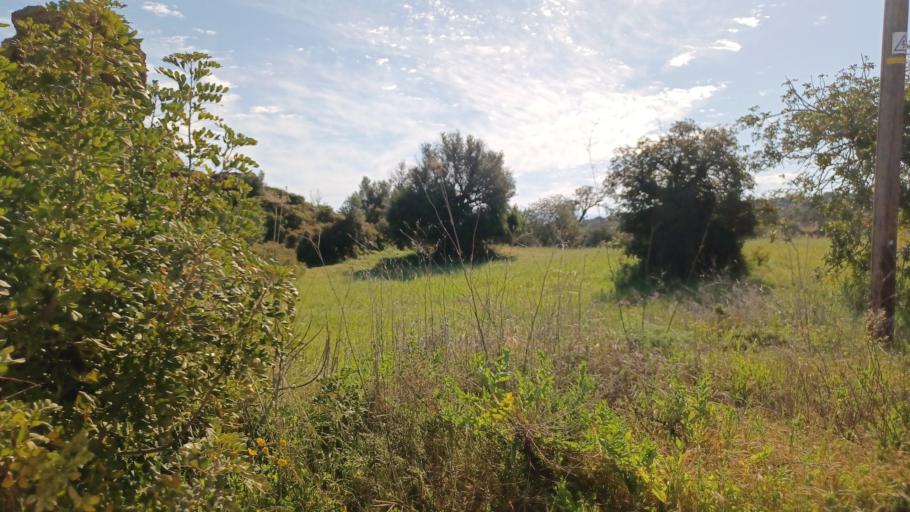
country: CY
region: Pafos
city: Polis
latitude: 35.0415
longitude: 32.3659
